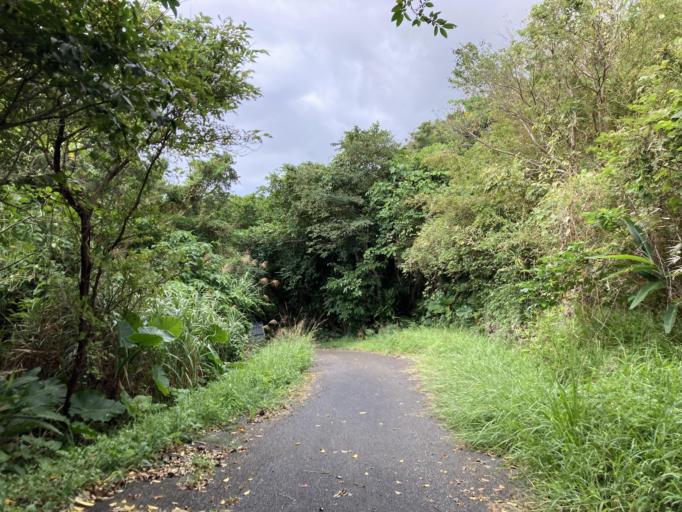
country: JP
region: Okinawa
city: Ginowan
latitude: 26.1613
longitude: 127.8128
